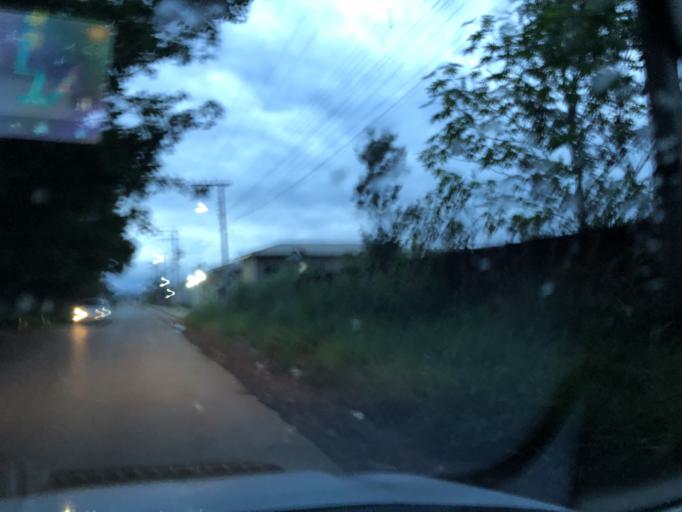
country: BR
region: Goias
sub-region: Luziania
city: Luziania
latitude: -16.1118
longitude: -47.9853
